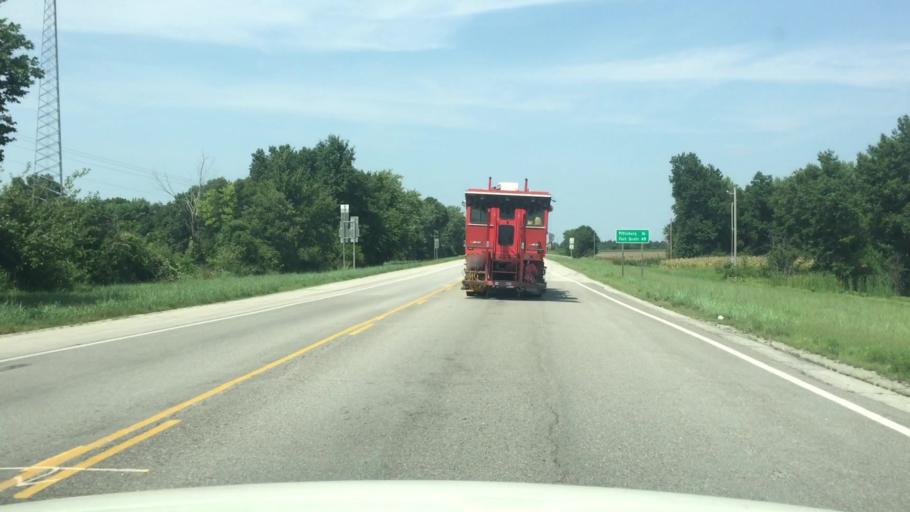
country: US
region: Kansas
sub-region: Cherokee County
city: Galena
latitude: 37.1808
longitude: -94.7045
